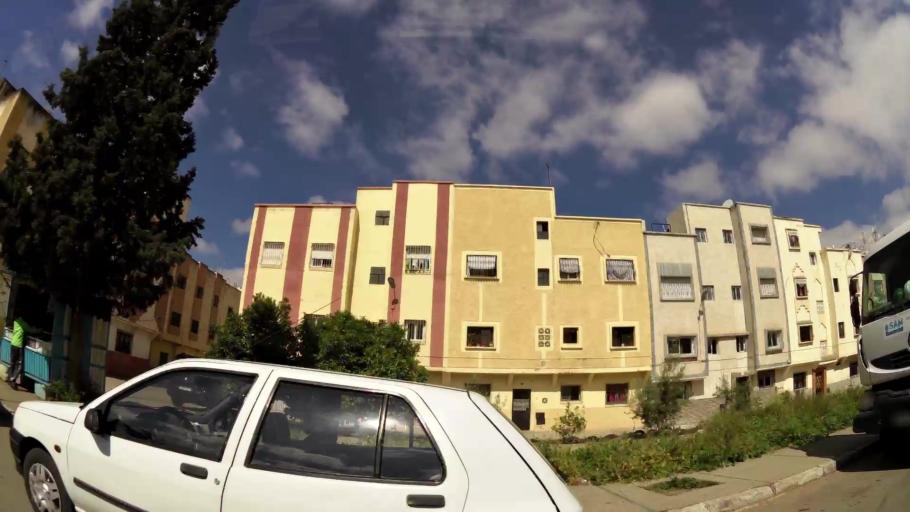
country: MA
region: Fes-Boulemane
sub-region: Fes
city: Fes
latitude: 34.0346
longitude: -5.0251
